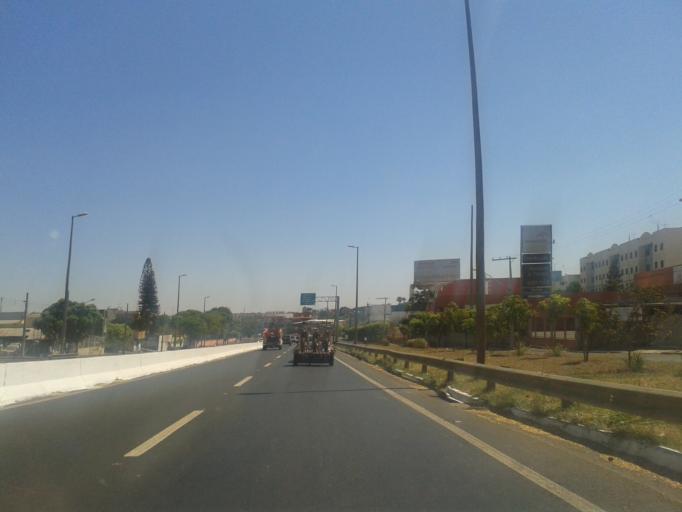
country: BR
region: Minas Gerais
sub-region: Uberlandia
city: Uberlandia
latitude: -18.9048
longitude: -48.2906
